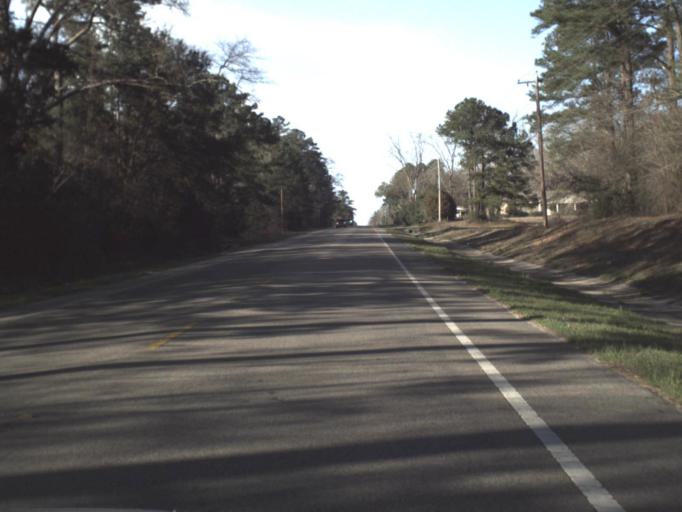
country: US
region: Florida
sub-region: Jackson County
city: Marianna
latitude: 30.7413
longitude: -85.2301
